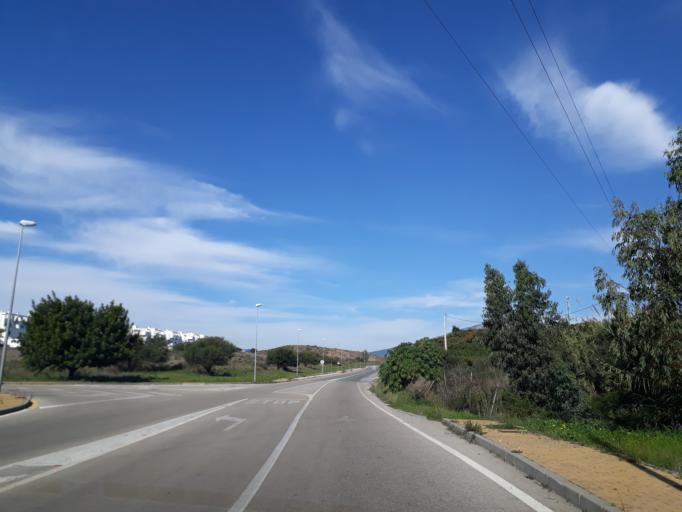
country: ES
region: Andalusia
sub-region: Provincia de Malaga
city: Fuengirola
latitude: 36.5264
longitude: -4.6858
